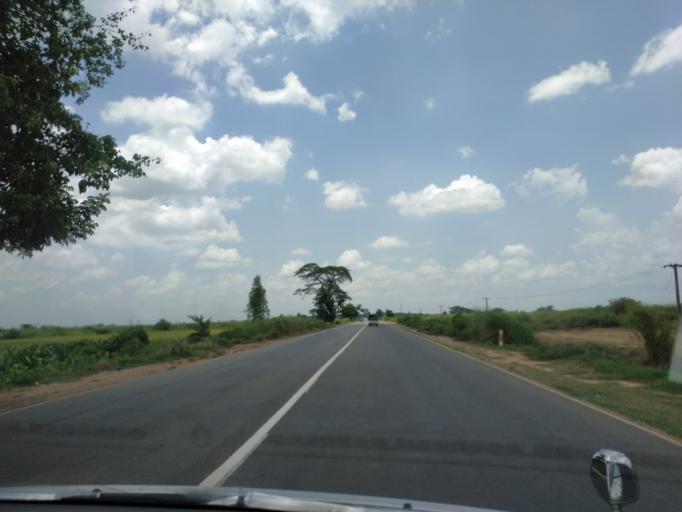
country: MM
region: Bago
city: Bago
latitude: 17.4697
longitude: 96.5612
